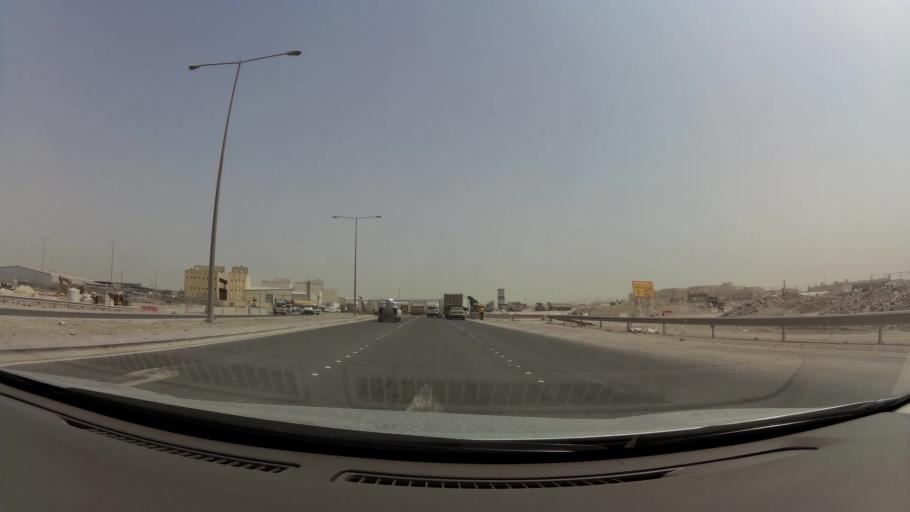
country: QA
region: Baladiyat ar Rayyan
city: Ar Rayyan
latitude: 25.1827
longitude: 51.4237
